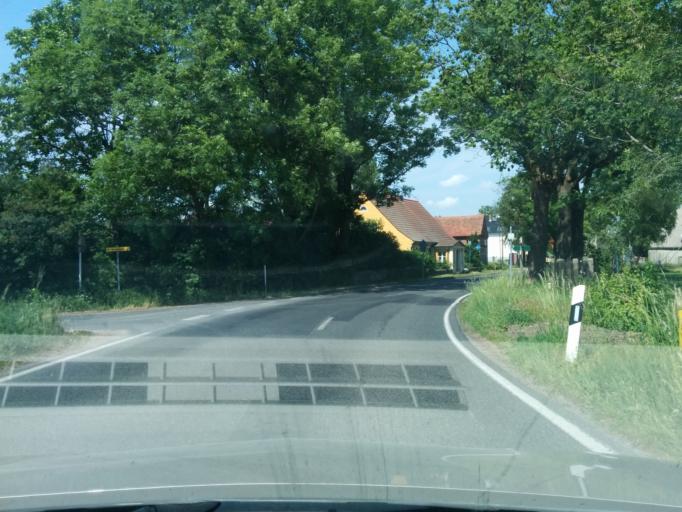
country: DE
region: Brandenburg
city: Ahrensfelde
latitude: 52.6234
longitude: 13.5760
